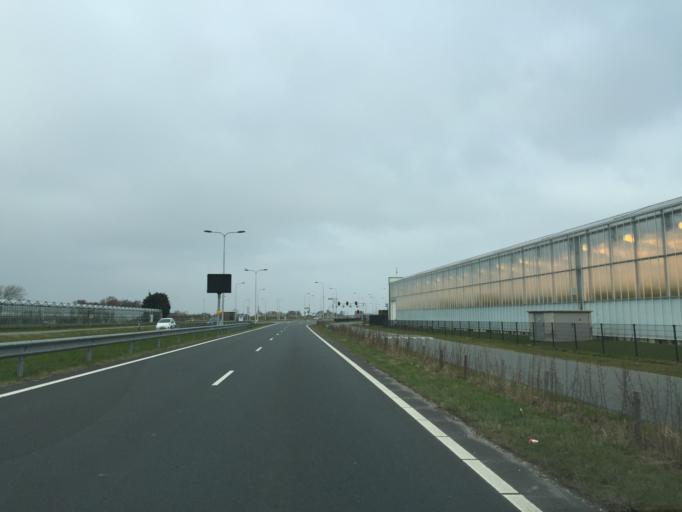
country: NL
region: South Holland
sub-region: Gemeente Rotterdam
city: Hoek van Holland
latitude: 51.9918
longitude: 4.1386
